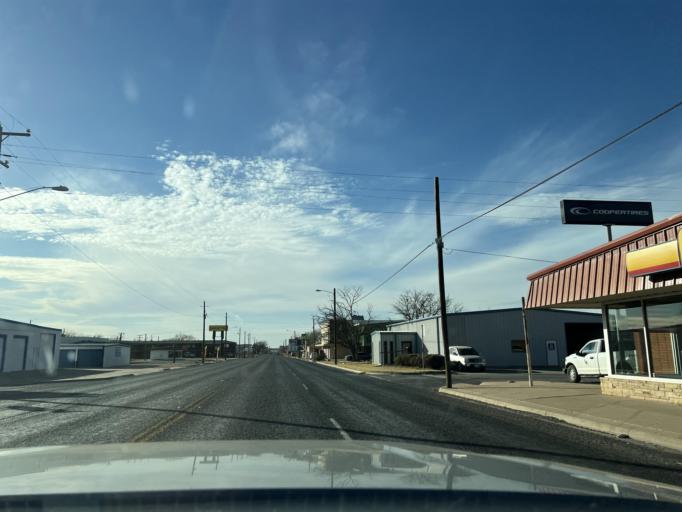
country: US
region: Texas
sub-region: Scurry County
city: Snyder
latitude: 32.7170
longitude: -100.9062
